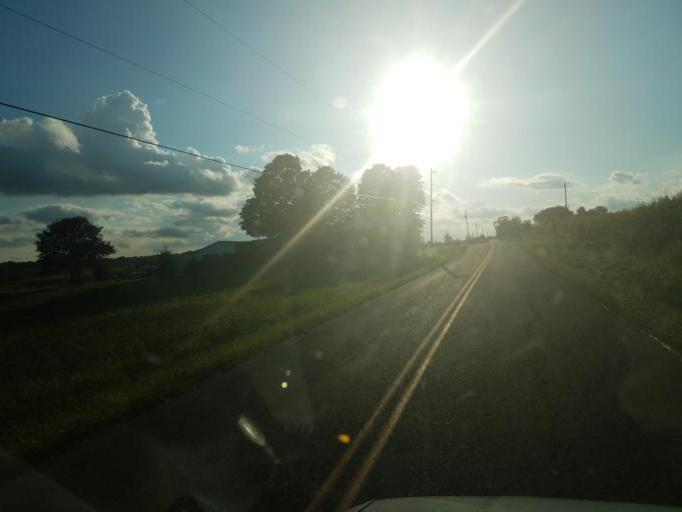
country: US
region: Ohio
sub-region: Knox County
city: Fredericktown
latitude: 40.4243
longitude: -82.6005
